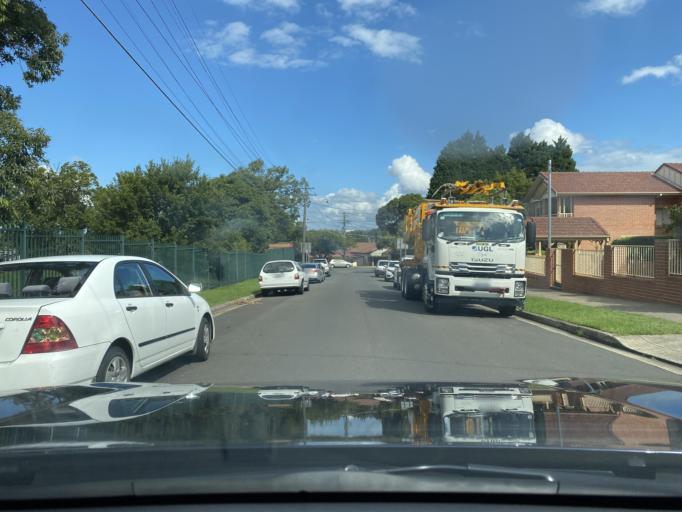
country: AU
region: New South Wales
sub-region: Canada Bay
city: Wareemba
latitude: -33.8691
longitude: 151.1327
